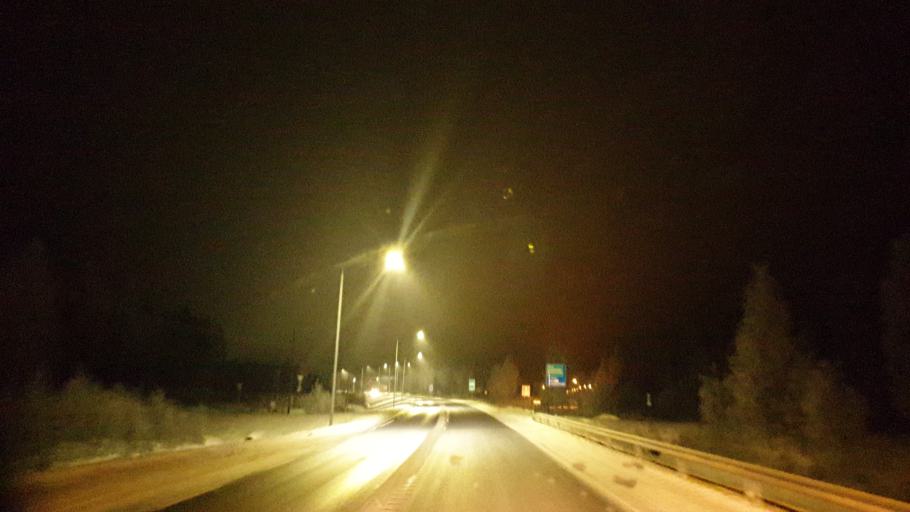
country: FI
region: Northern Ostrobothnia
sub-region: Oulunkaari
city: Ii
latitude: 65.2698
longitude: 25.3628
